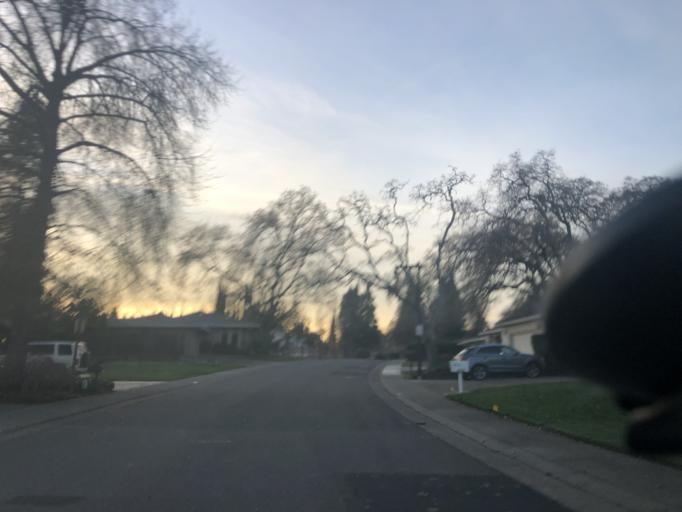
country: US
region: California
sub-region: Sacramento County
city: Gold River
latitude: 38.6421
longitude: -121.2278
